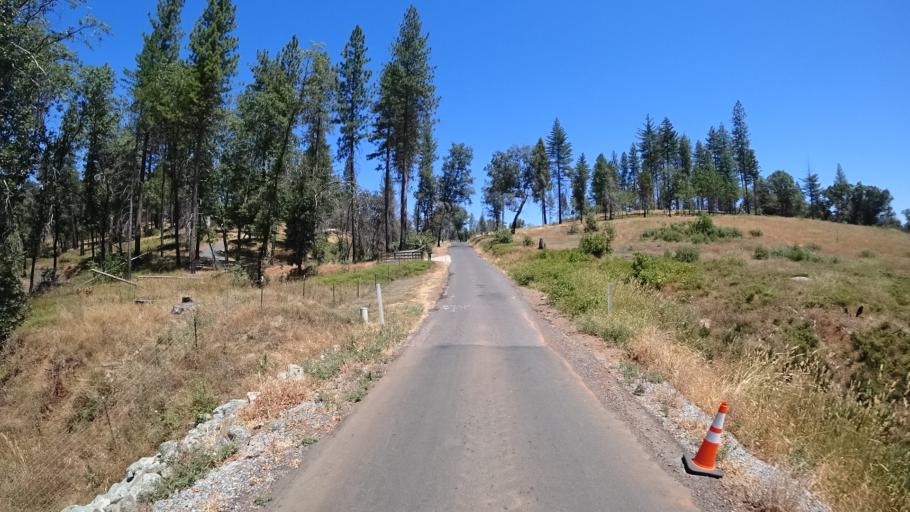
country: US
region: California
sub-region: Calaveras County
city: Mountain Ranch
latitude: 38.2407
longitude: -120.5732
